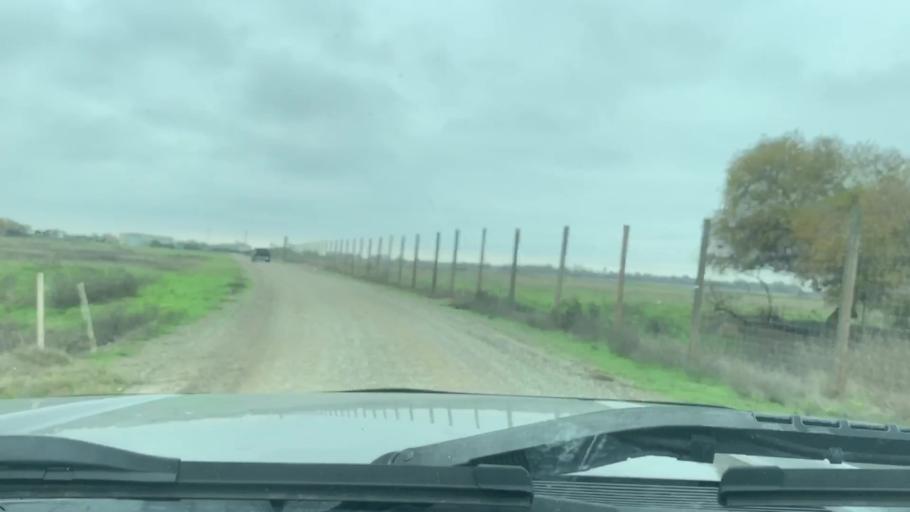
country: US
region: California
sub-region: Merced County
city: Los Banos
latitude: 37.1843
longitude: -120.7976
